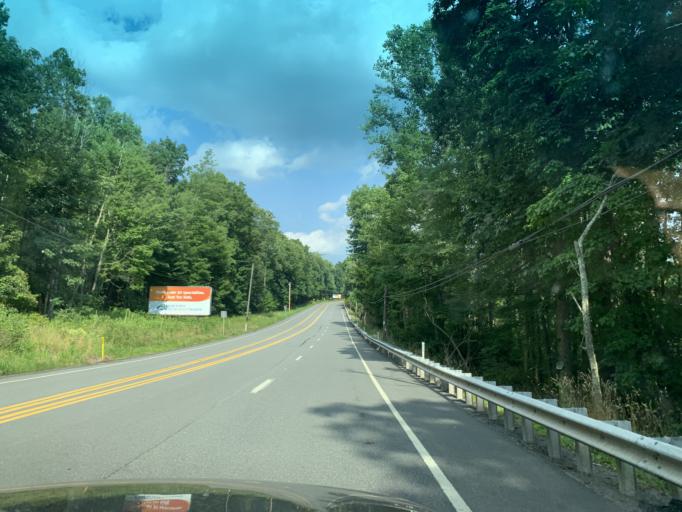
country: US
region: Pennsylvania
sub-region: Schuylkill County
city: Girardville
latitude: 40.7769
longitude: -76.2808
